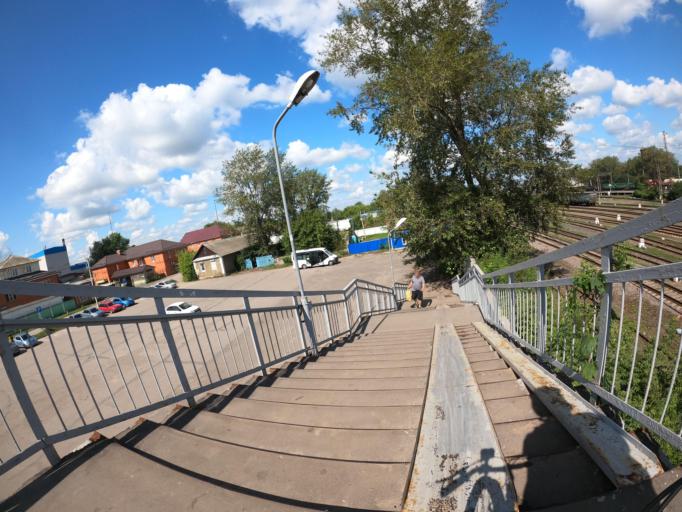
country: RU
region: Moskovskaya
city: Lopatinskiy
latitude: 55.3121
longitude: 38.7013
